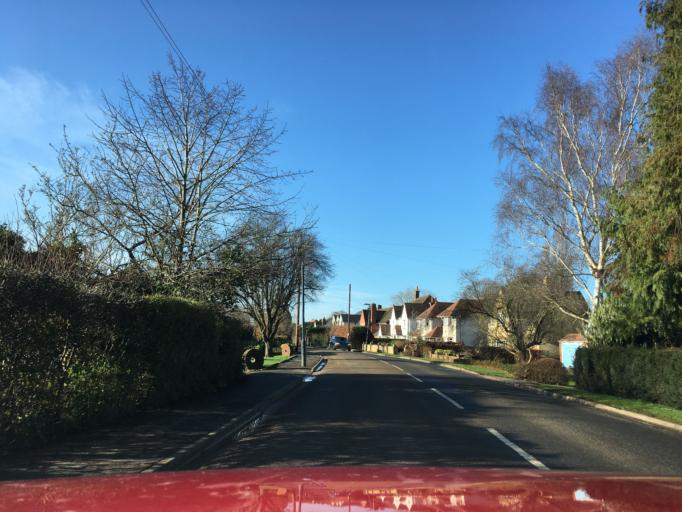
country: GB
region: England
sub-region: Warwickshire
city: Stratford-upon-Avon
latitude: 52.1901
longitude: -1.6795
